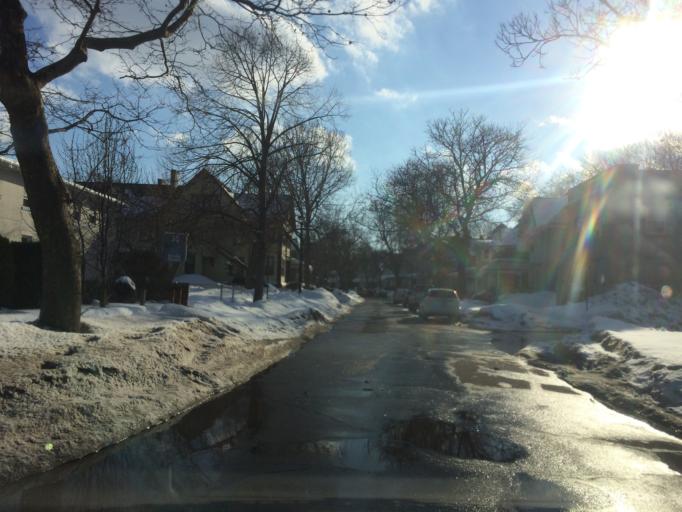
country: US
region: New York
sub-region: Monroe County
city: Rochester
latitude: 43.1451
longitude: -77.5914
